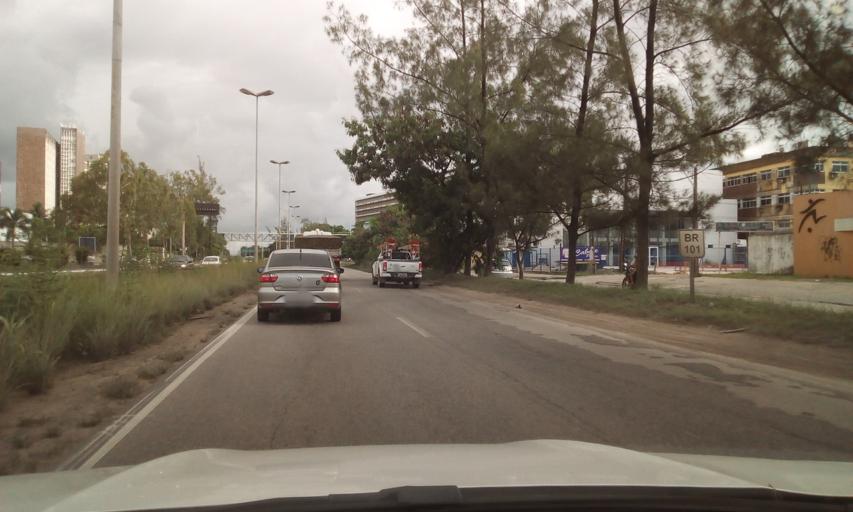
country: BR
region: Pernambuco
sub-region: Recife
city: Recife
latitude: -8.0446
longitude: -34.9442
